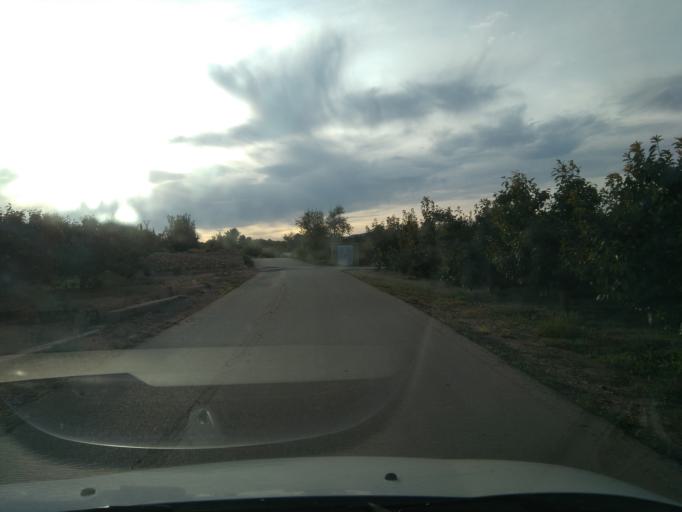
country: ES
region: Valencia
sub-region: Provincia de Valencia
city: Benimodo
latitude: 39.2002
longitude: -0.5684
